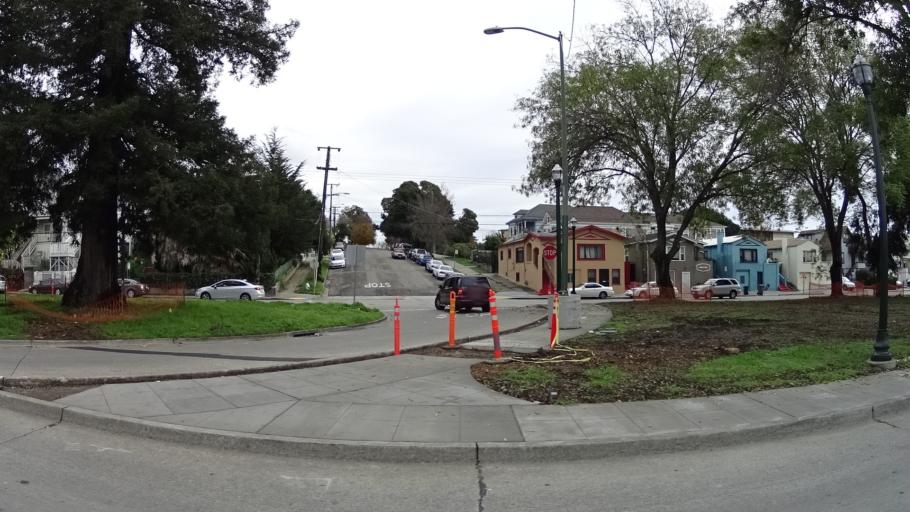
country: US
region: California
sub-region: Alameda County
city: Alameda
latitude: 37.7917
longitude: -122.2431
